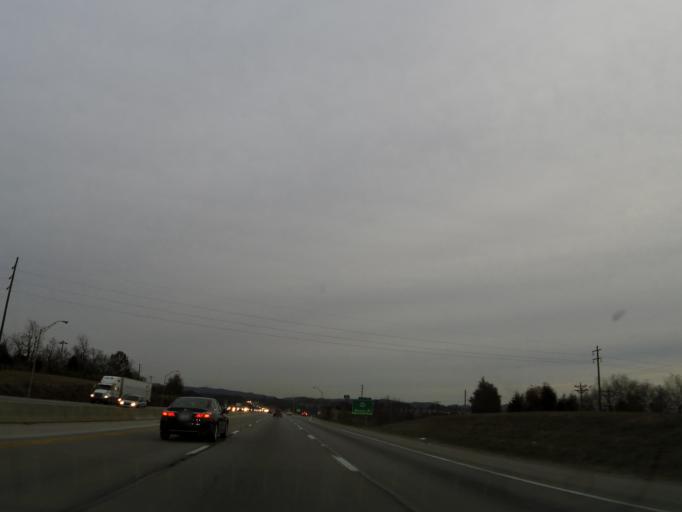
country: US
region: Kentucky
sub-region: Madison County
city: Berea
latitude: 37.6028
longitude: -84.3146
